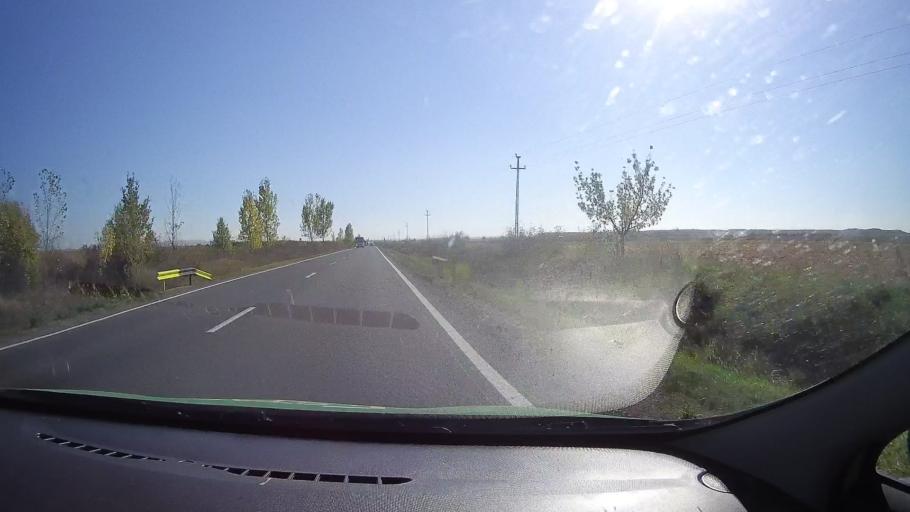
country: RO
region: Satu Mare
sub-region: Oras Ardud
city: Madaras
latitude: 47.6621
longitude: 22.8726
